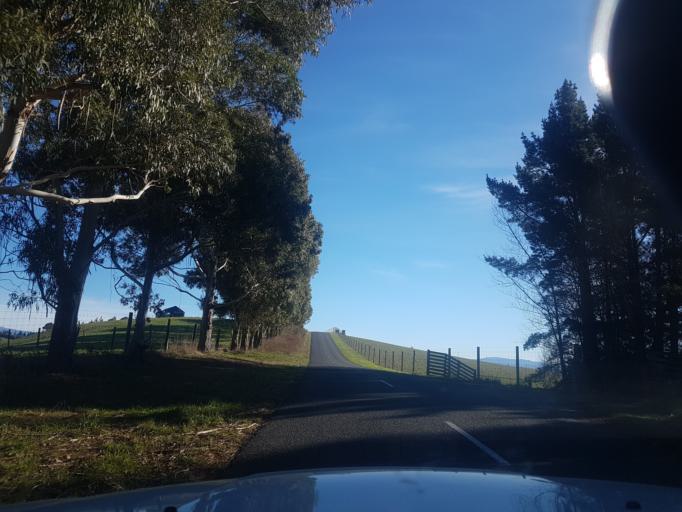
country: NZ
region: Canterbury
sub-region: Timaru District
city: Pleasant Point
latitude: -44.2477
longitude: 171.0826
